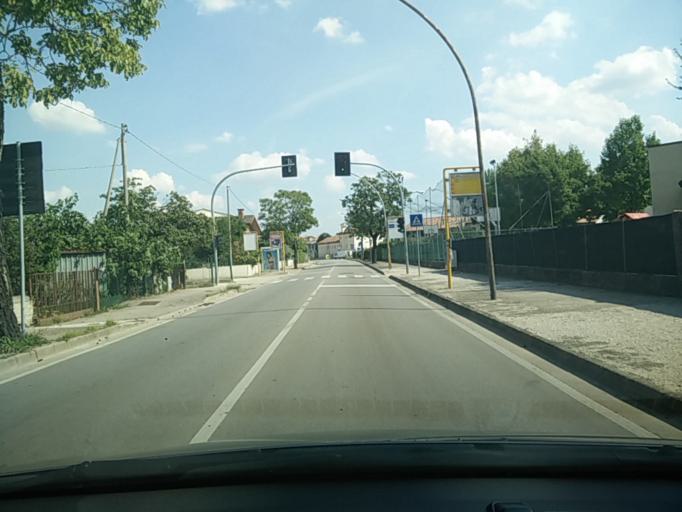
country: IT
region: Veneto
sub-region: Provincia di Treviso
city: Salvatronda
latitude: 45.6753
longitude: 11.9765
